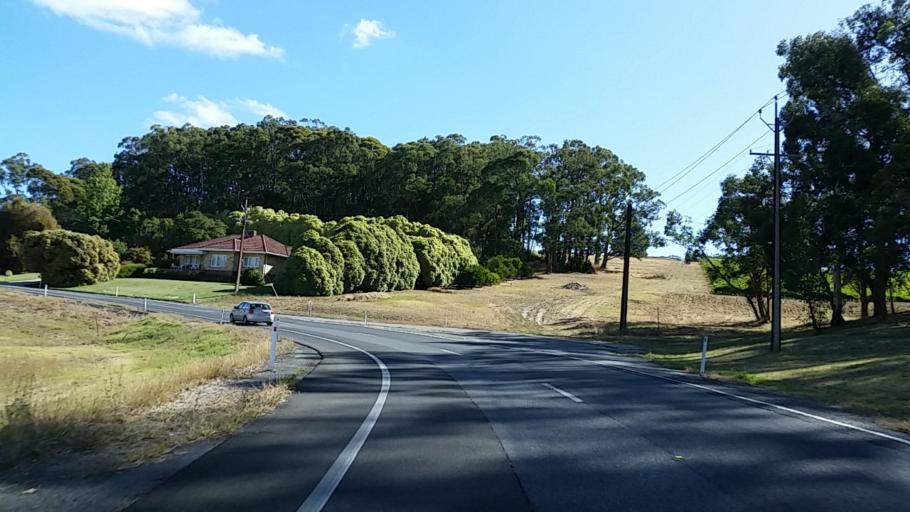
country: AU
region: South Australia
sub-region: Adelaide Hills
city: Bridgewater
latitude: -34.9724
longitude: 138.7306
